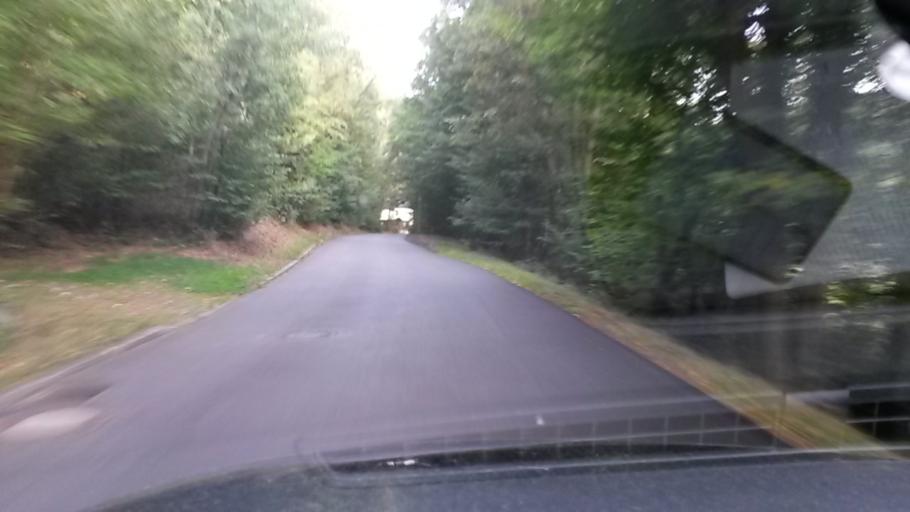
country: DE
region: North Rhine-Westphalia
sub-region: Regierungsbezirk Arnsberg
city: Herscheid
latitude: 51.2247
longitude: 7.7297
